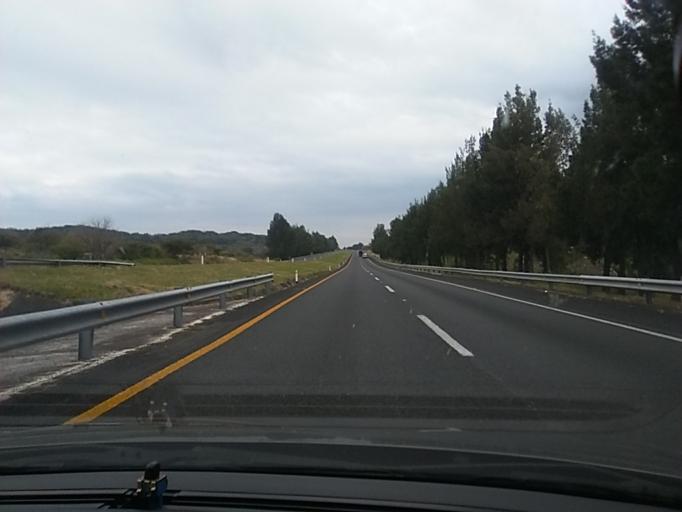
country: MX
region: Michoacan
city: Penjamillo de Degollado
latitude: 20.0882
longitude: -102.0041
